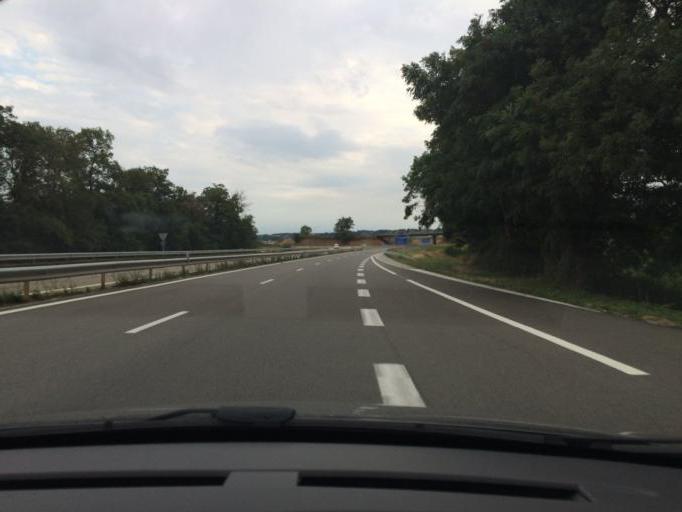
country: FR
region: Rhone-Alpes
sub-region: Departement du Rhone
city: Saint-Laurent-de-Mure
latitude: 45.6991
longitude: 5.0716
